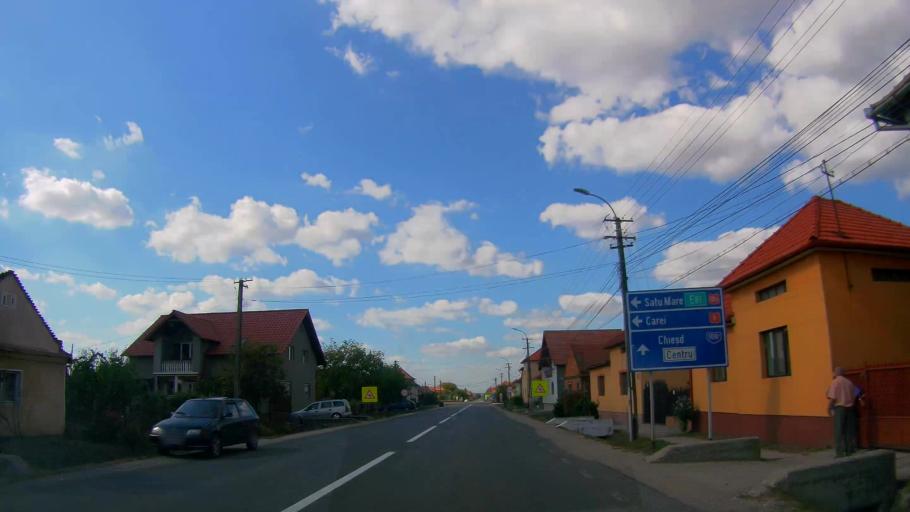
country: RO
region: Salaj
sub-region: Comuna Sarmasag
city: Sarmasag
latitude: 47.3404
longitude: 22.8337
